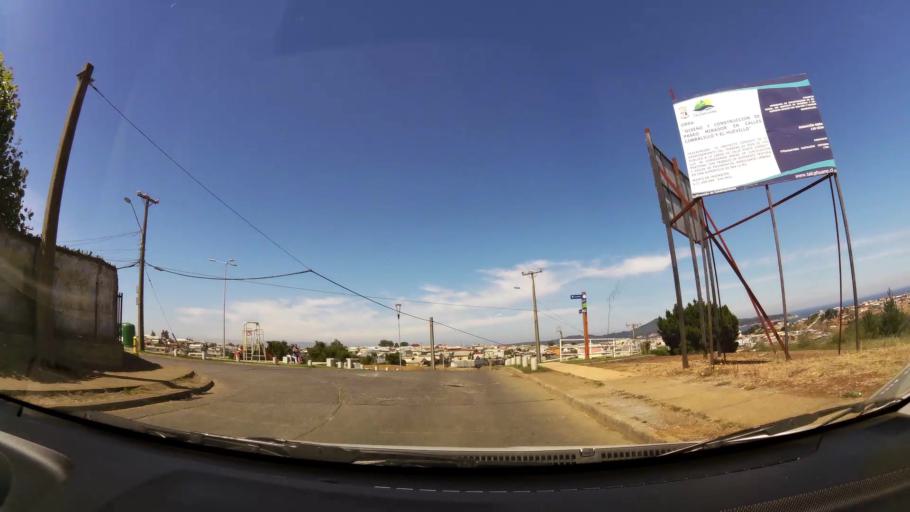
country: CL
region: Biobio
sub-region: Provincia de Concepcion
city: Talcahuano
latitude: -36.7165
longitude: -73.1411
